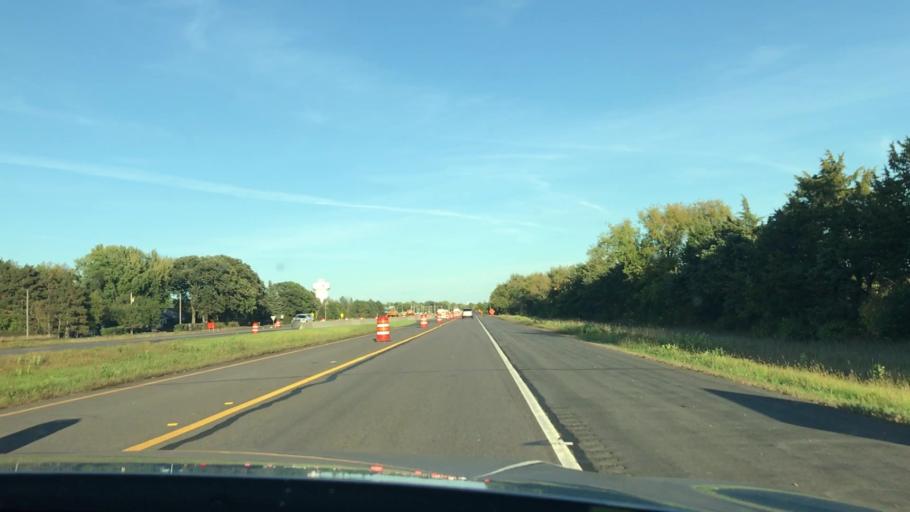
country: US
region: Minnesota
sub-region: Wright County
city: Otsego
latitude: 45.3060
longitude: -93.6180
